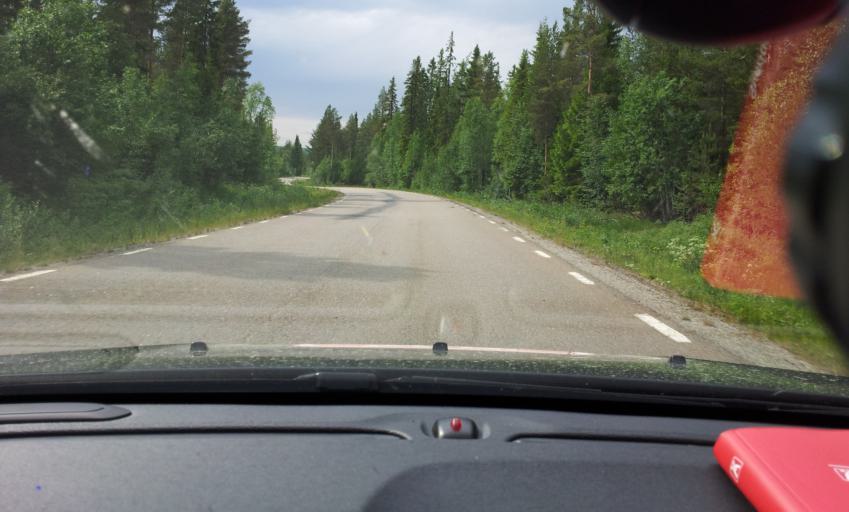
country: SE
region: Jaemtland
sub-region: Bergs Kommun
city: Hoverberg
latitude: 62.6615
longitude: 14.7749
